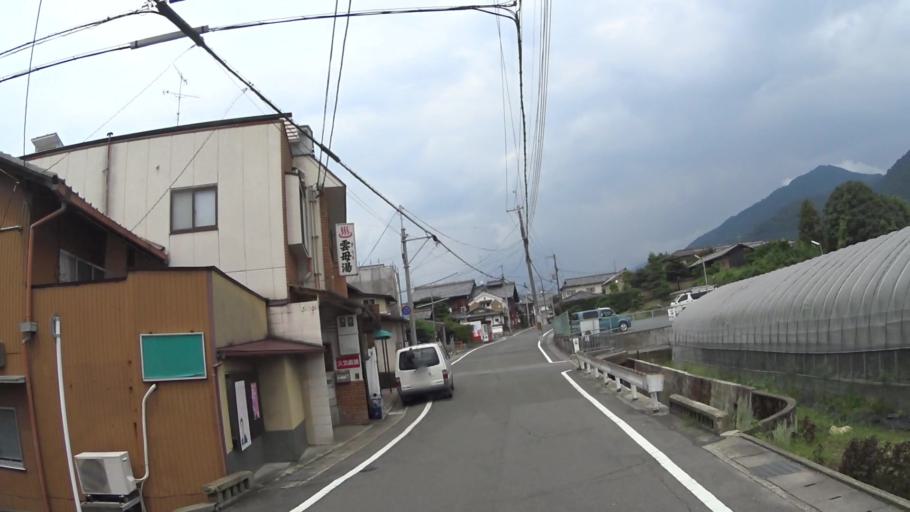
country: JP
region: Kyoto
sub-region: Kyoto-shi
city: Kamigyo-ku
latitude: 35.0455
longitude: 135.7941
